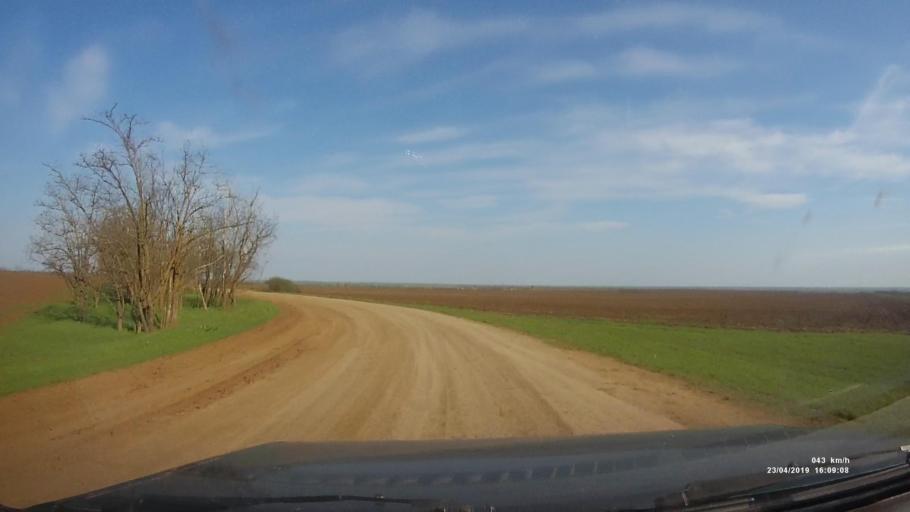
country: RU
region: Rostov
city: Remontnoye
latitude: 46.4818
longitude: 43.1081
